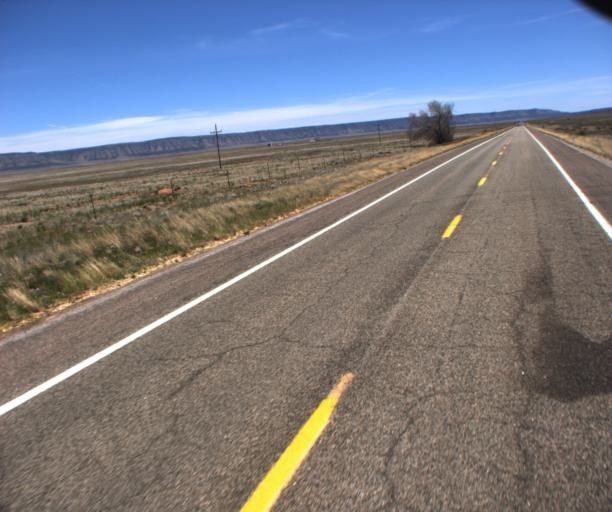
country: US
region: Arizona
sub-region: Mohave County
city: Peach Springs
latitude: 35.4779
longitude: -113.1371
